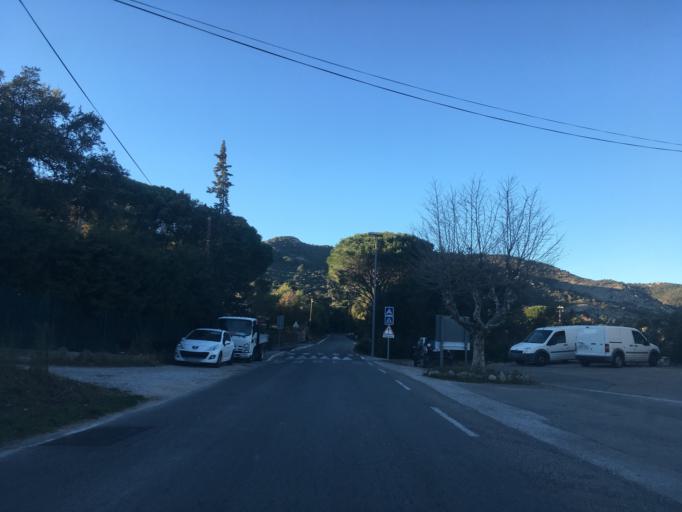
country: FR
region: Provence-Alpes-Cote d'Azur
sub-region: Departement du Var
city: Le Plan-de-la-Tour
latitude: 43.3333
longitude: 6.5480
